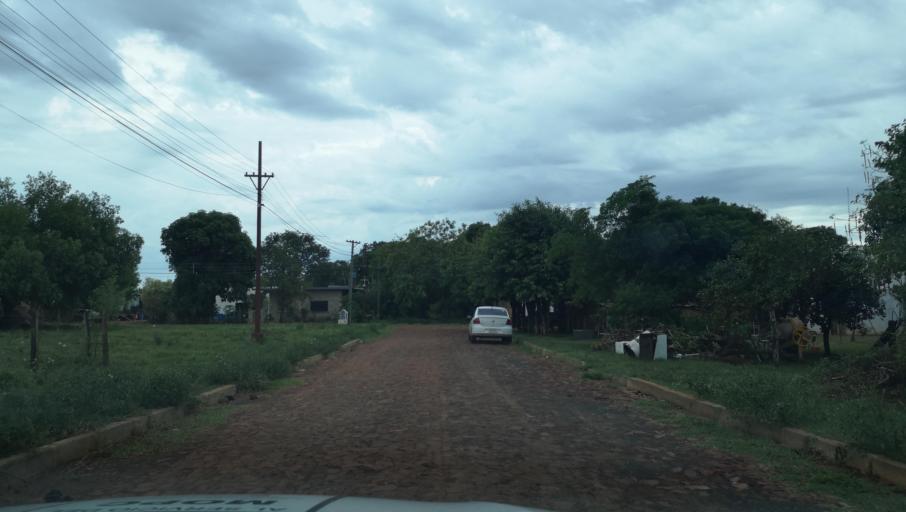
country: PY
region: Misiones
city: Santa Maria
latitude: -26.8843
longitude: -57.0390
